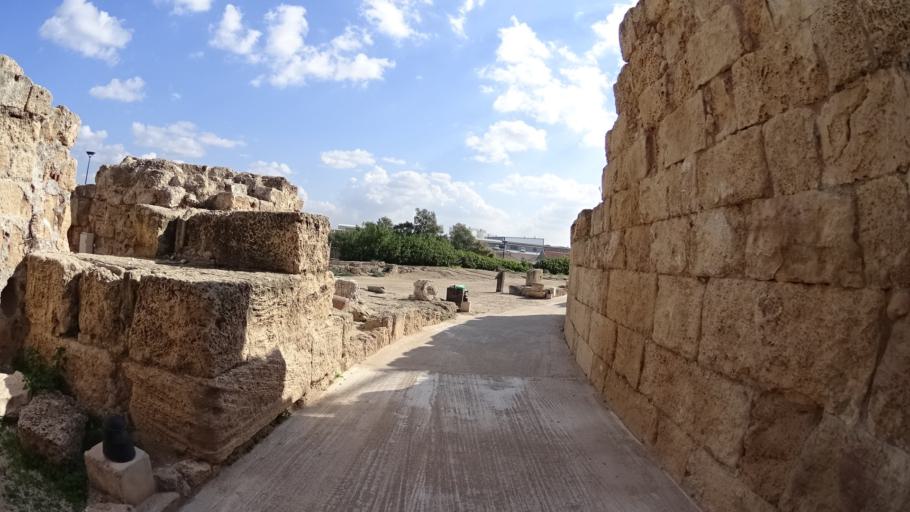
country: IL
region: Haifa
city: Qesarya
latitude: 32.4963
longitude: 34.8913
